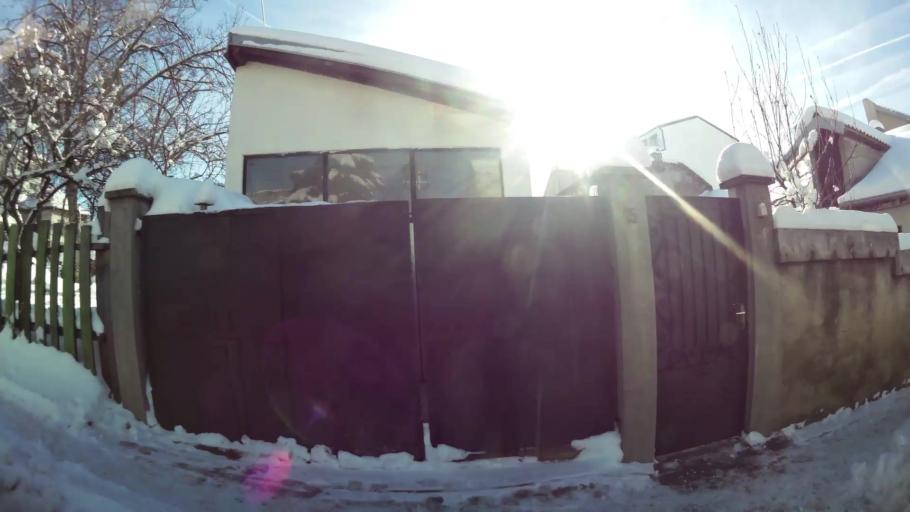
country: RS
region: Central Serbia
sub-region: Belgrade
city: Palilula
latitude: 44.7908
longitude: 20.5073
